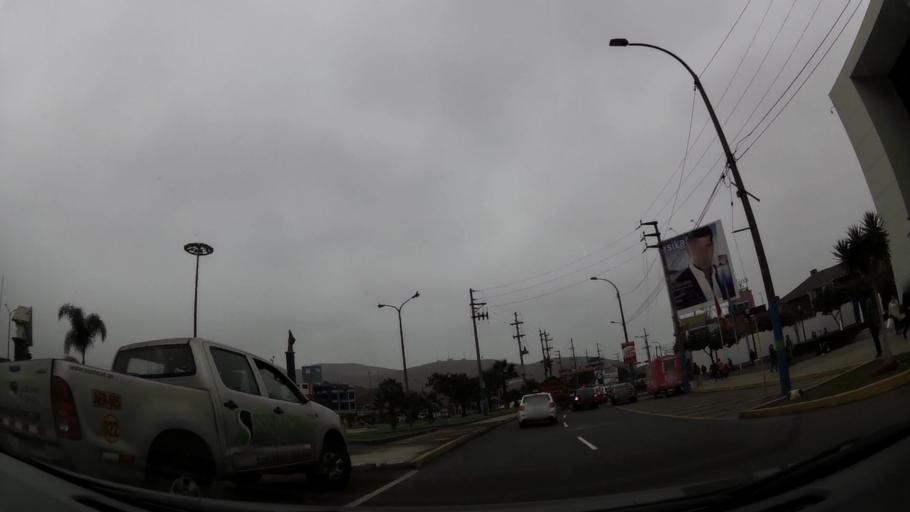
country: PE
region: Lima
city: Ventanilla
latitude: -11.8772
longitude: -77.1277
